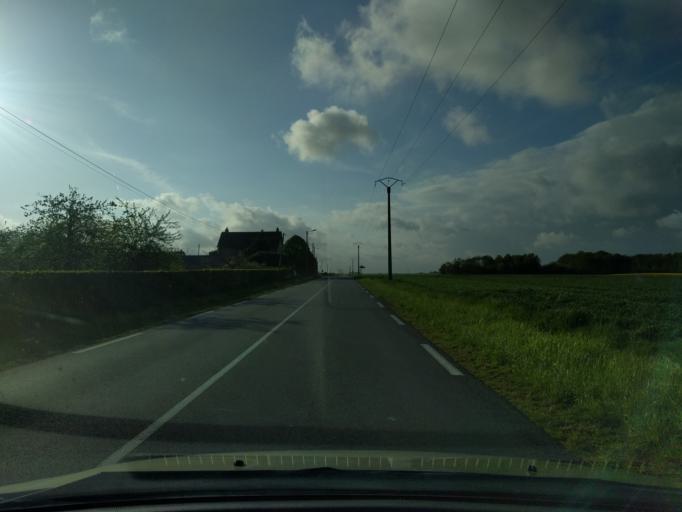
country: FR
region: Haute-Normandie
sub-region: Departement de l'Eure
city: Conches-en-Ouche
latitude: 48.9356
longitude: 0.9795
